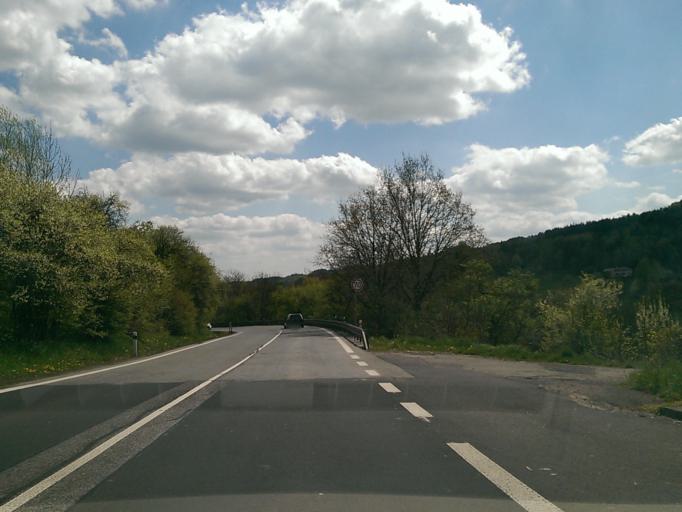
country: CZ
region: Liberecky
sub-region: Okres Semily
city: Turnov
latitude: 50.5763
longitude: 15.1626
